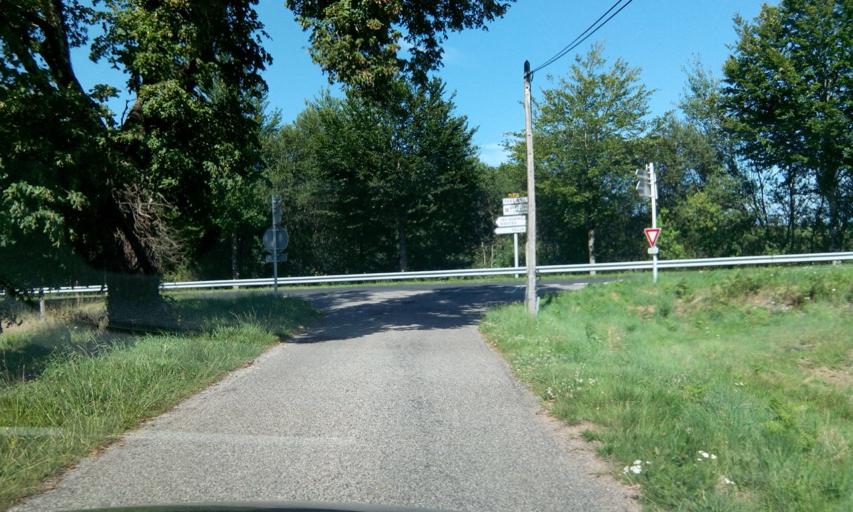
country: FR
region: Limousin
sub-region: Departement de la Correze
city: Beynat
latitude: 45.0833
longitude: 1.7807
